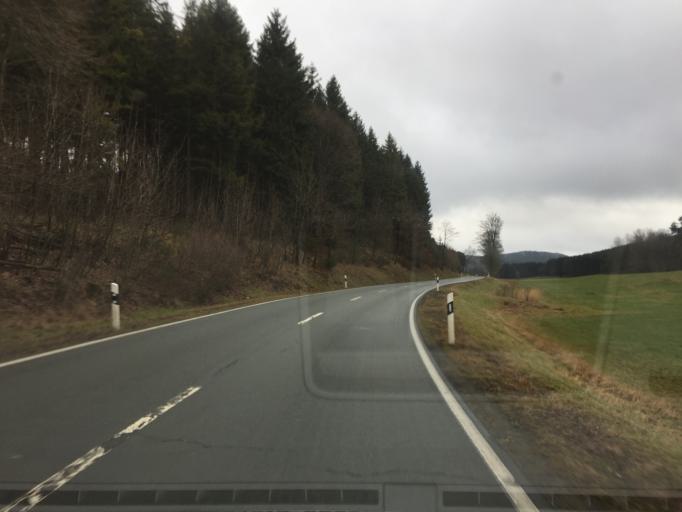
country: DE
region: North Rhine-Westphalia
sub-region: Regierungsbezirk Arnsberg
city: Winterberg
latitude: 51.2270
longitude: 8.5792
